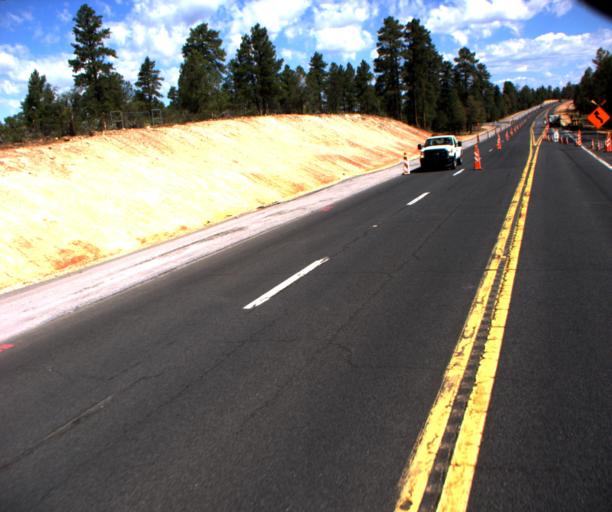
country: US
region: Arizona
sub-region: Coconino County
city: Grand Canyon Village
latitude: 35.9550
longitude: -112.1318
